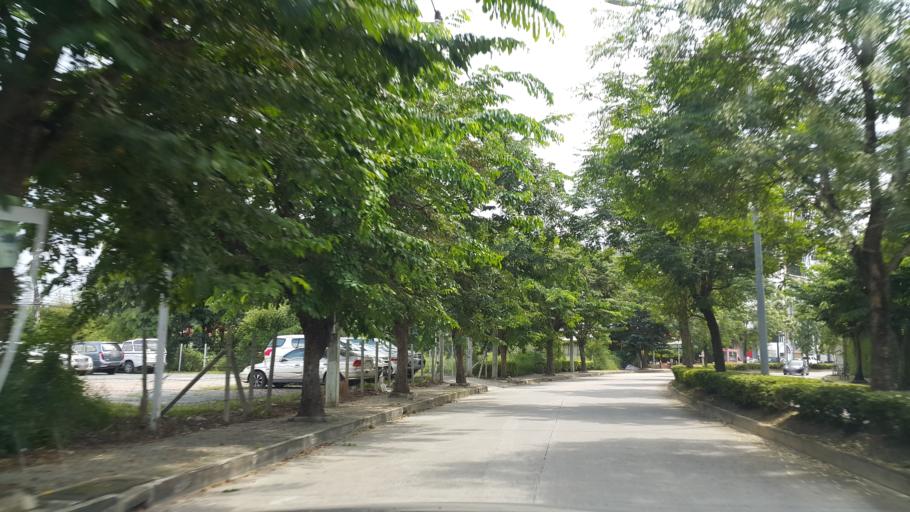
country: TH
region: Chiang Mai
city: Chiang Mai
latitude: 18.8062
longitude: 99.0239
